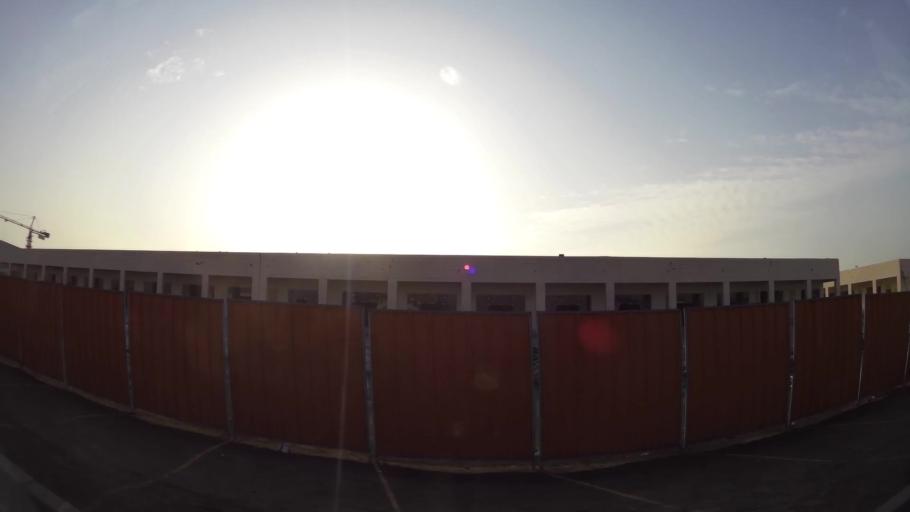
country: AE
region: Abu Dhabi
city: Abu Dhabi
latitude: 24.3450
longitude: 54.5123
